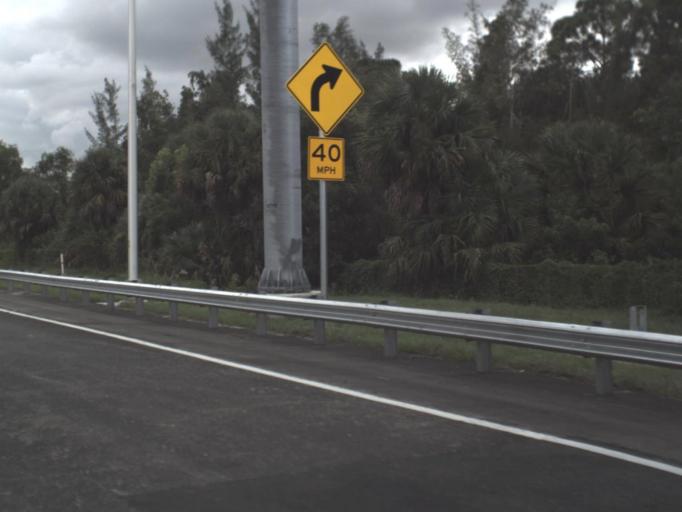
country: US
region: Florida
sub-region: Palm Beach County
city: Plantation Mobile Home Park
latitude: 26.7151
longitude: -80.1370
